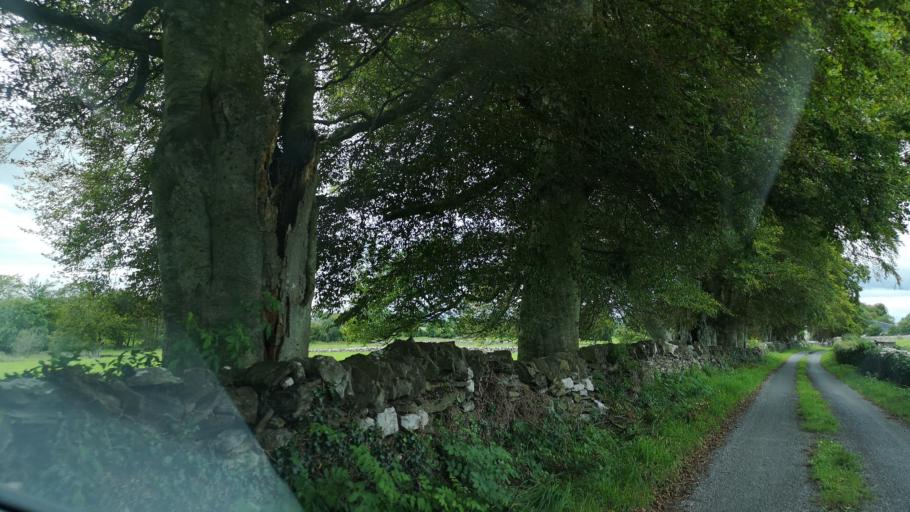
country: IE
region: Connaught
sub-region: County Galway
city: Loughrea
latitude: 53.1656
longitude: -8.4518
